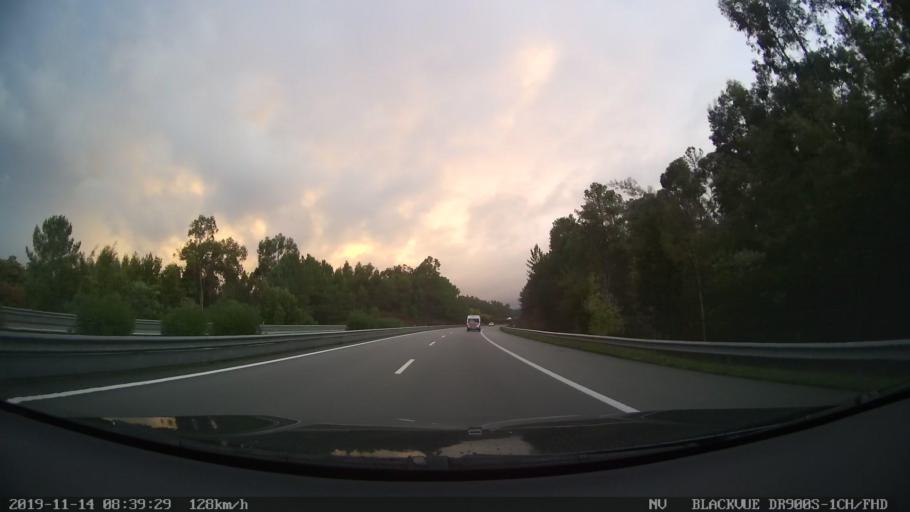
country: PT
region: Viana do Castelo
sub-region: Ponte de Lima
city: Ponte de Lima
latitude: 41.7313
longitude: -8.5624
